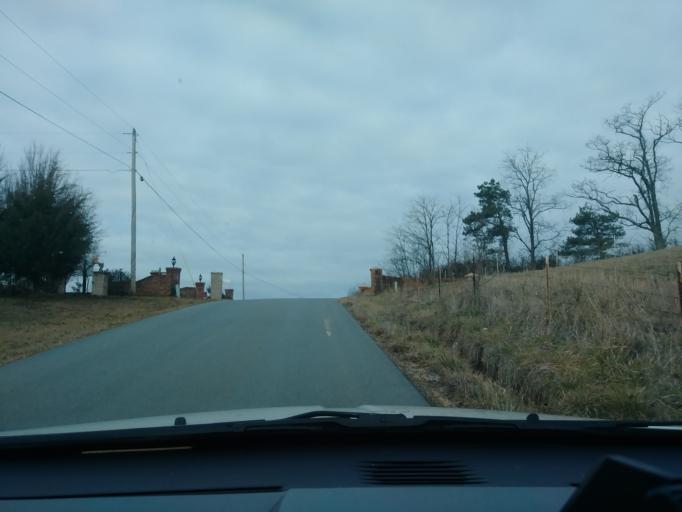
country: US
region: Tennessee
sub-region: Greene County
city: Mosheim
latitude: 36.1069
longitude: -82.9134
